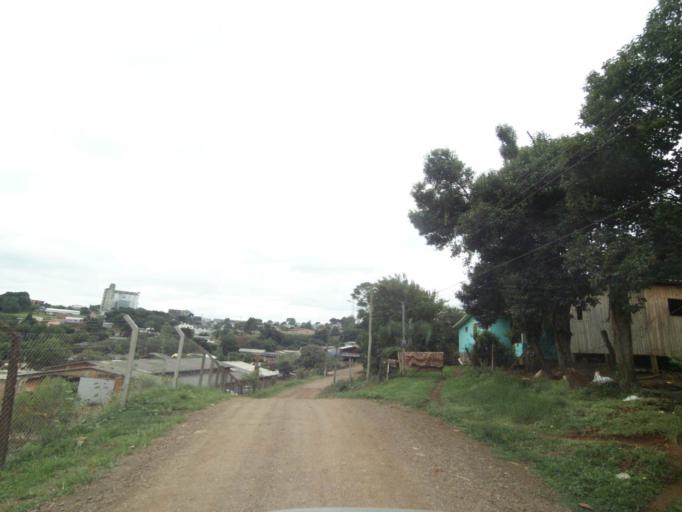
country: BR
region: Rio Grande do Sul
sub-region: Lagoa Vermelha
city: Lagoa Vermelha
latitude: -28.2150
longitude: -51.5405
